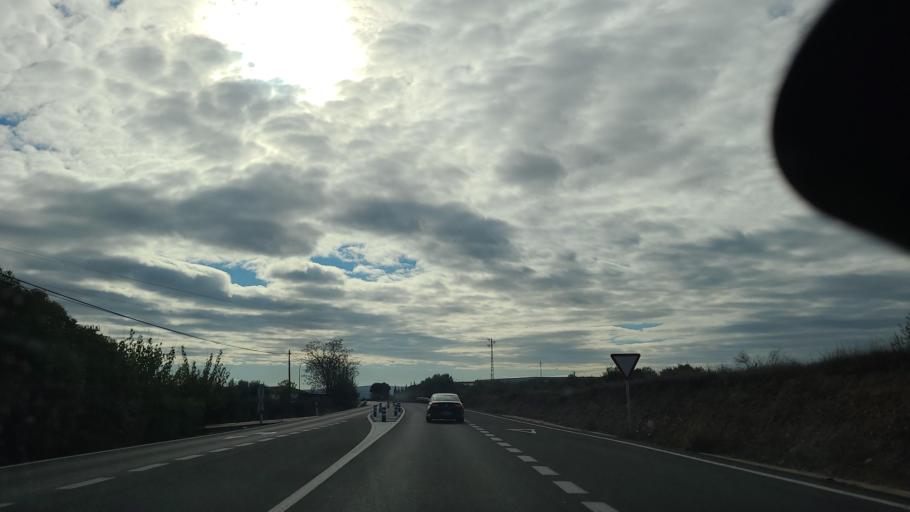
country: ES
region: Andalusia
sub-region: Provincia de Jaen
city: Villanueva de la Reina
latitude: 38.0426
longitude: -3.9128
